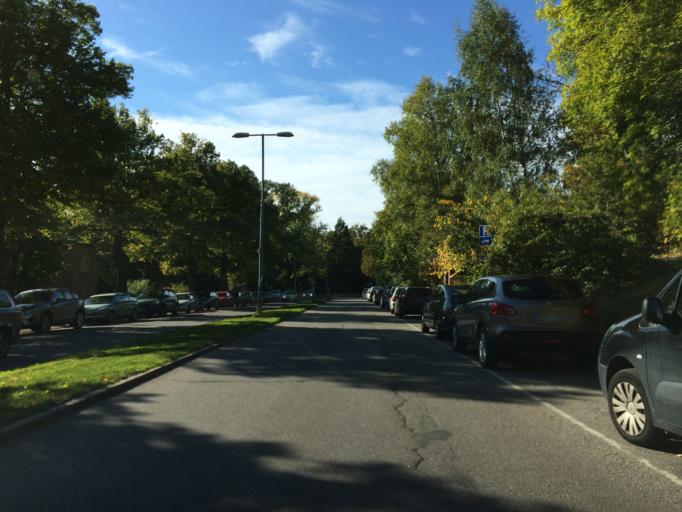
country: SE
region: Stockholm
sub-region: Stockholms Kommun
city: OEstermalm
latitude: 59.3332
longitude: 18.1028
